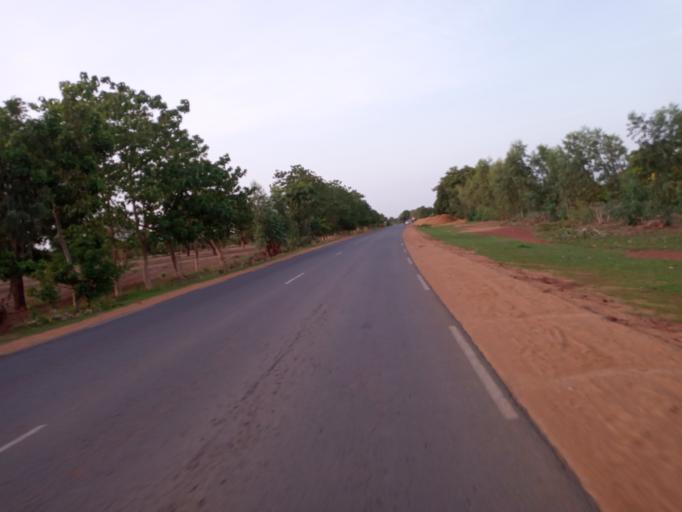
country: ML
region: Bamako
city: Bamako
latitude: 12.2860
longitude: -8.1746
